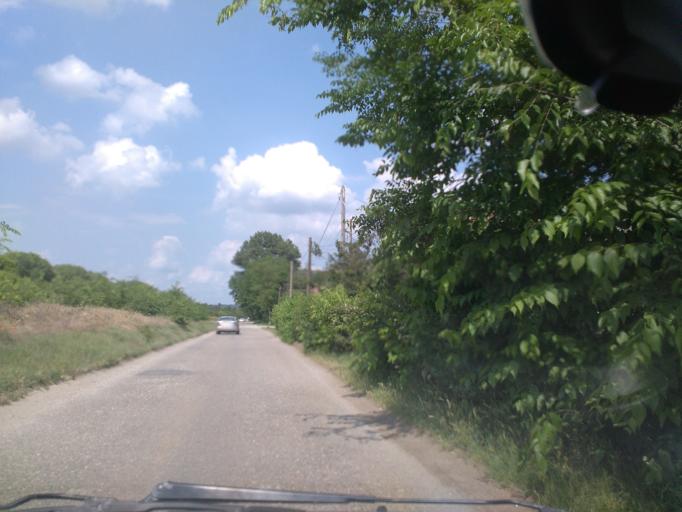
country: HU
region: Pest
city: Veresegyhaz
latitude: 47.6423
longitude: 19.2666
